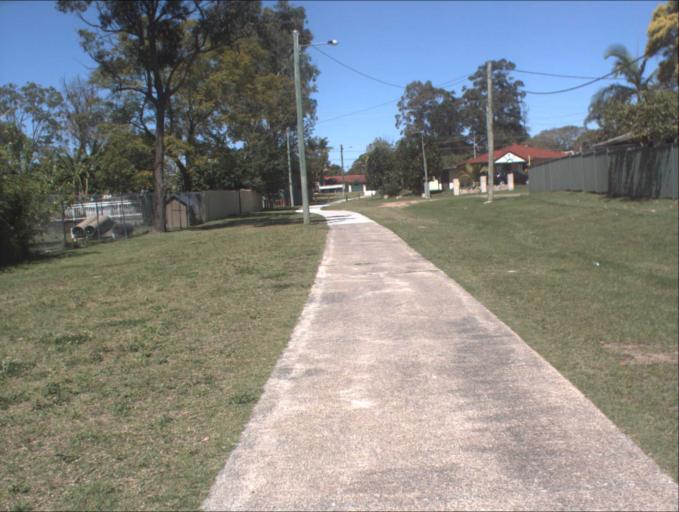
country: AU
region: Queensland
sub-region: Logan
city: Waterford West
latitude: -27.6807
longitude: 153.1072
